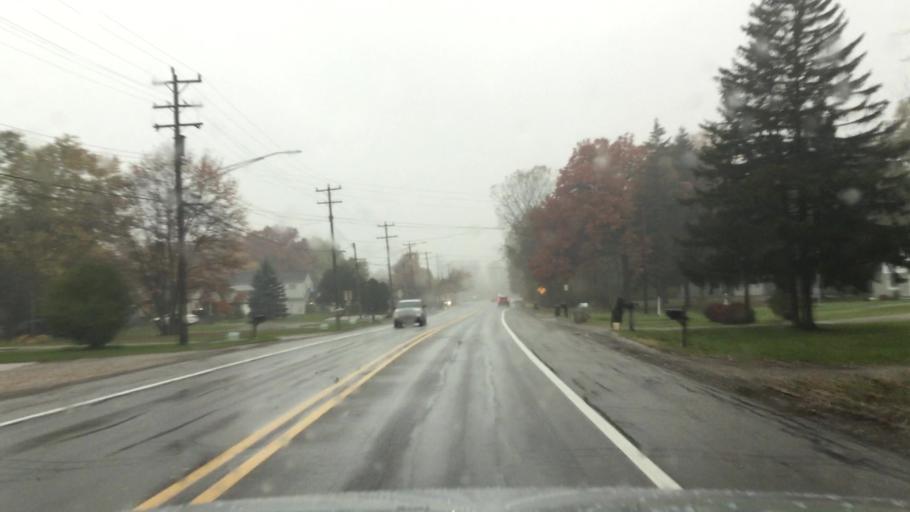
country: US
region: Michigan
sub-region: Macomb County
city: New Baltimore
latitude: 42.6872
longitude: -82.7139
